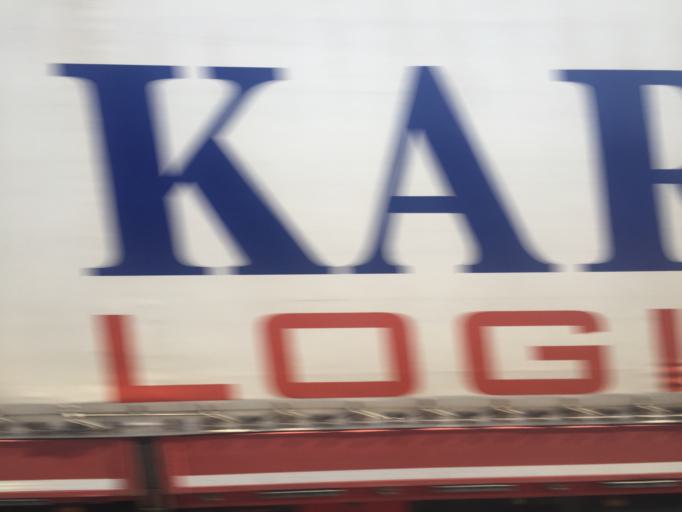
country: TR
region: Bursa
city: Demirtas
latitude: 40.2696
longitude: 29.0525
